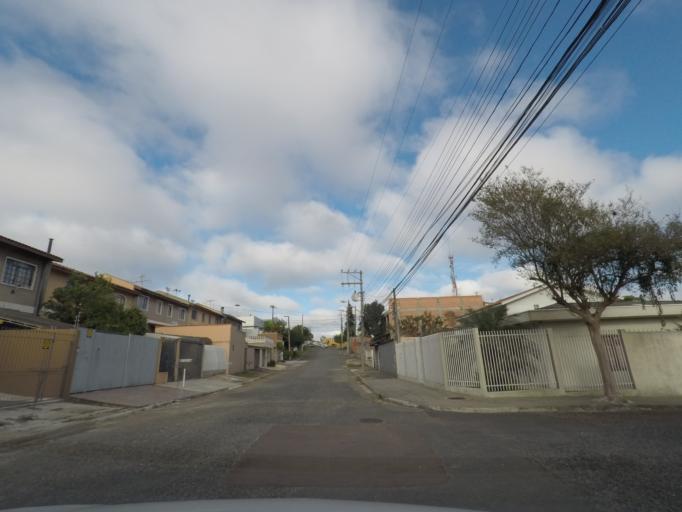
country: BR
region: Parana
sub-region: Pinhais
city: Pinhais
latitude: -25.4597
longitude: -49.2366
